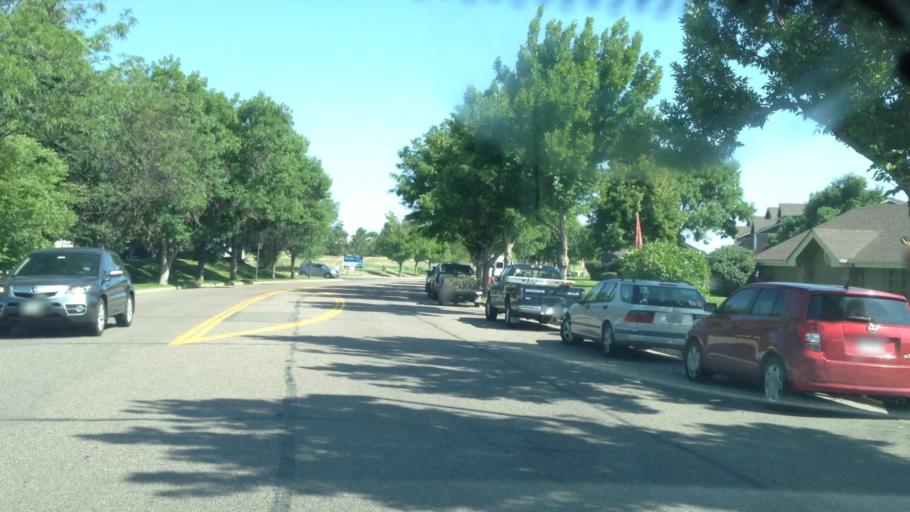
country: US
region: Colorado
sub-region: Adams County
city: Aurora
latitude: 39.7231
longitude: -104.8072
